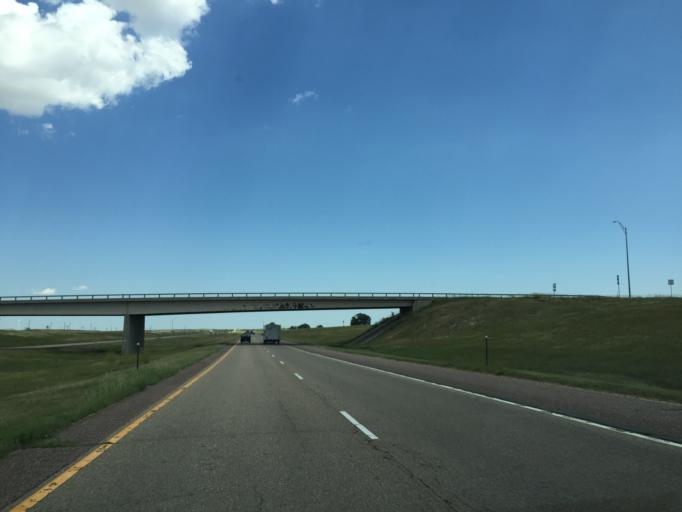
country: US
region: Colorado
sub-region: Lincoln County
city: Hugo
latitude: 39.2787
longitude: -103.3988
